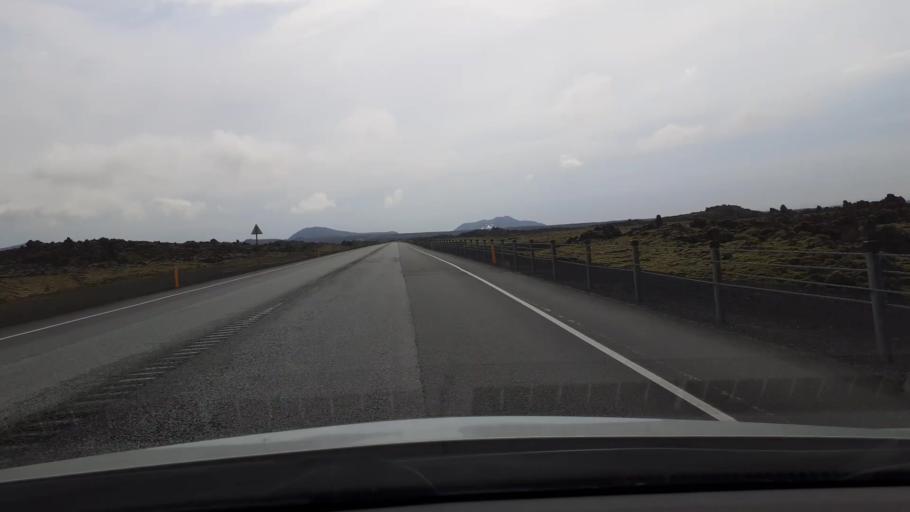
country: IS
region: Southern Peninsula
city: Vogar
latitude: 63.9381
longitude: -22.4276
